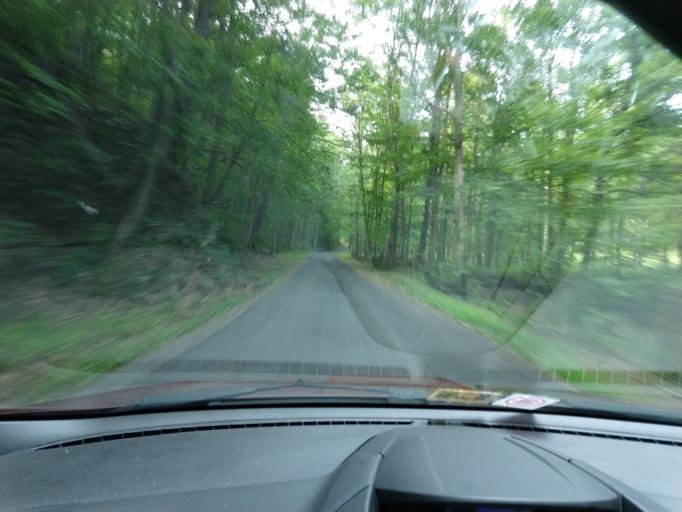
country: US
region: Virginia
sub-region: City of Covington
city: Covington
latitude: 37.8994
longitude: -80.0852
